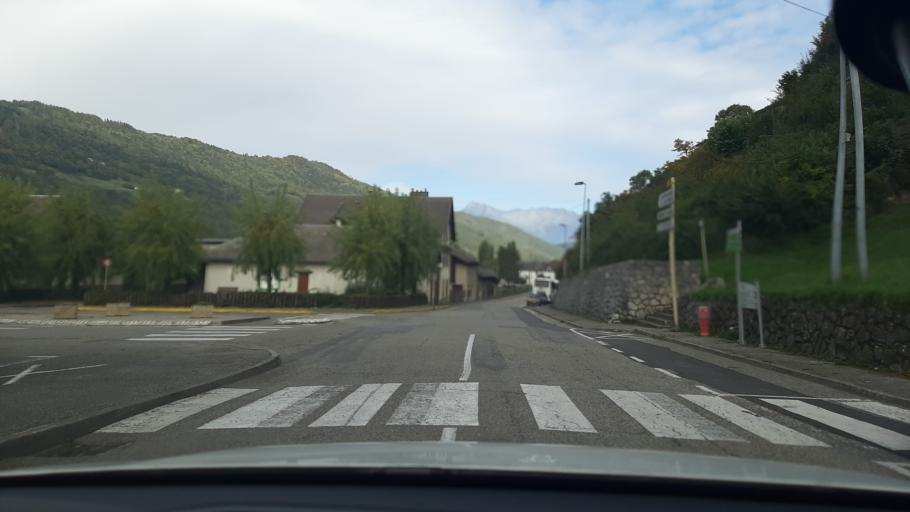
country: FR
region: Rhone-Alpes
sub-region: Departement de la Savoie
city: La Rochette
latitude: 45.4579
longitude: 6.1203
